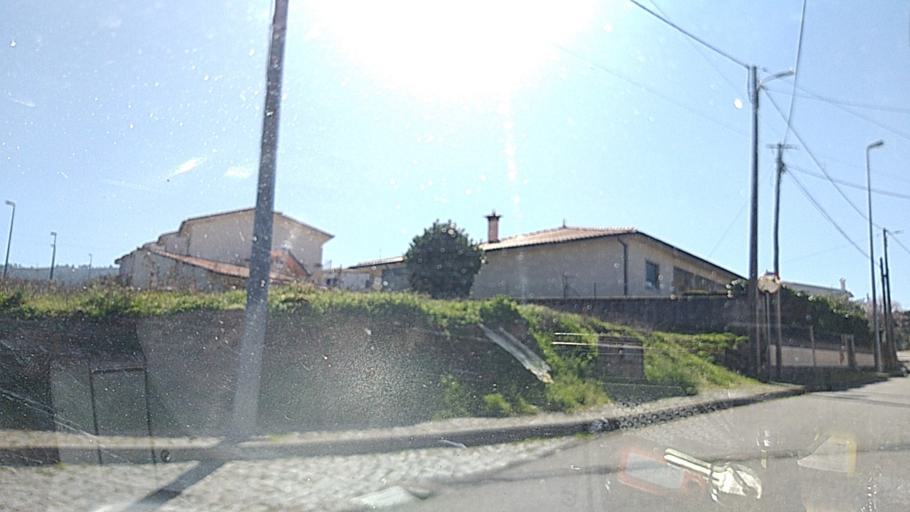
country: PT
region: Guarda
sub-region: Celorico da Beira
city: Celorico da Beira
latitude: 40.6187
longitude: -7.4066
